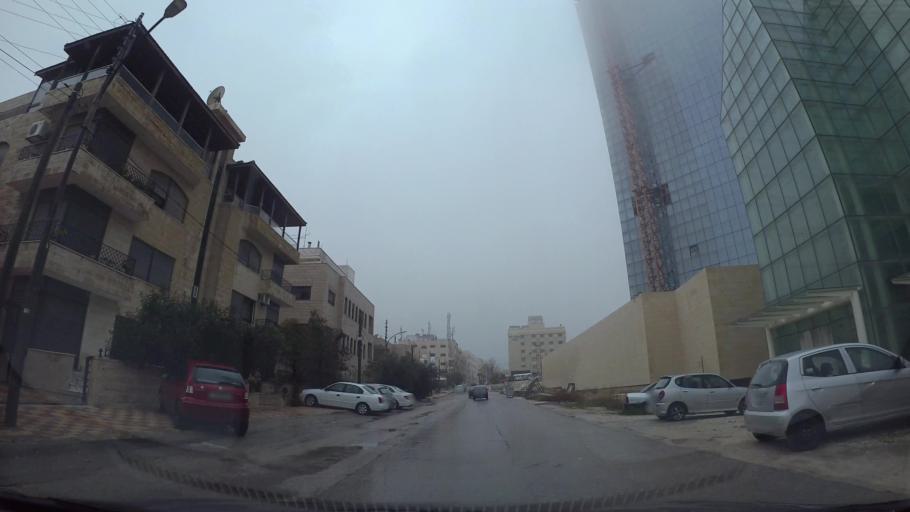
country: JO
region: Amman
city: Wadi as Sir
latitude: 31.9625
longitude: 35.8684
